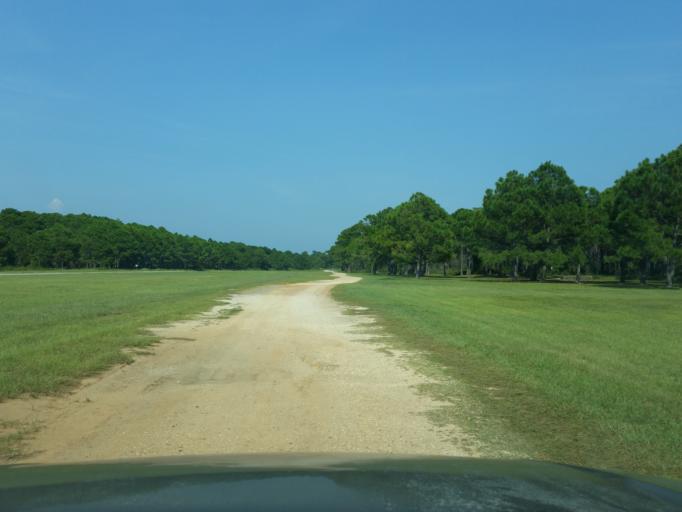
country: US
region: Alabama
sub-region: Mobile County
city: Dauphin Island
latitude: 30.2291
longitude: -88.0175
